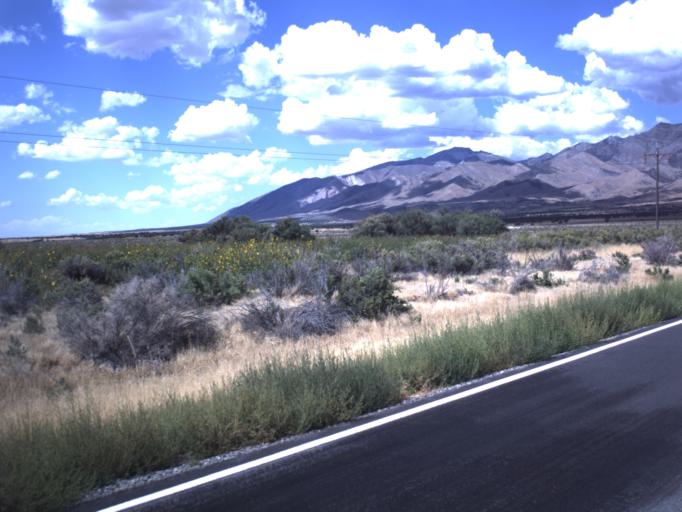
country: US
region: Utah
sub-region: Tooele County
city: Grantsville
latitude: 40.2857
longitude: -112.6650
